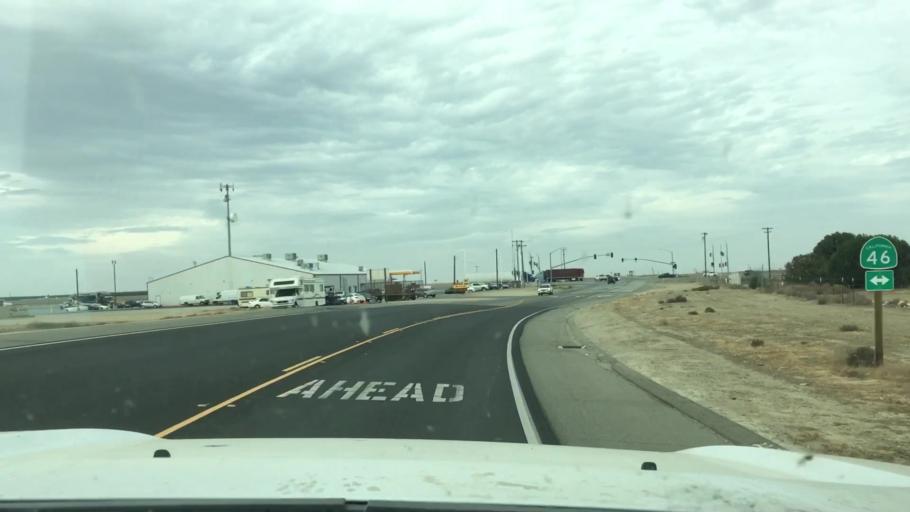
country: US
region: California
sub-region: Kern County
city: Lost Hills
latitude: 35.6126
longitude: -119.8675
